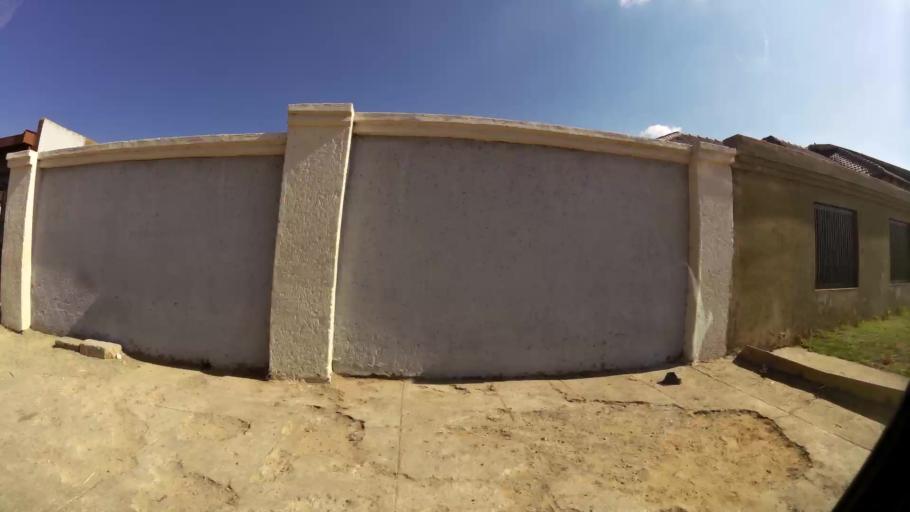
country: ZA
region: Gauteng
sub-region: City of Johannesburg Metropolitan Municipality
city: Soweto
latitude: -26.2345
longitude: 27.8866
